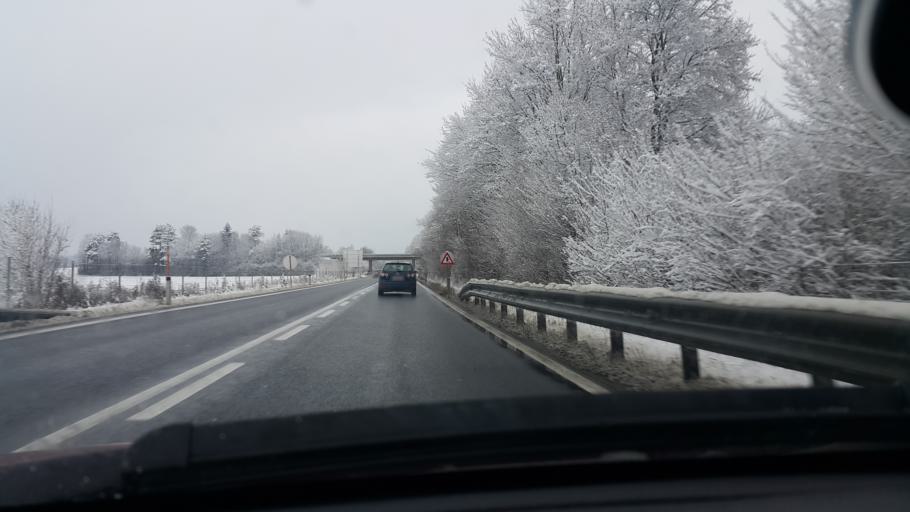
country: AT
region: Styria
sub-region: Politischer Bezirk Voitsberg
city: Mooskirchen
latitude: 46.9843
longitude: 15.2720
